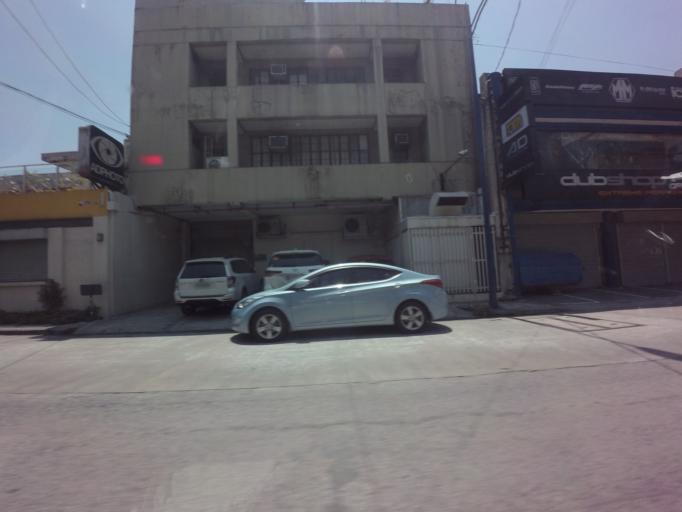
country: PH
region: Metro Manila
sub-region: Makati City
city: Makati City
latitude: 14.5583
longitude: 121.0016
